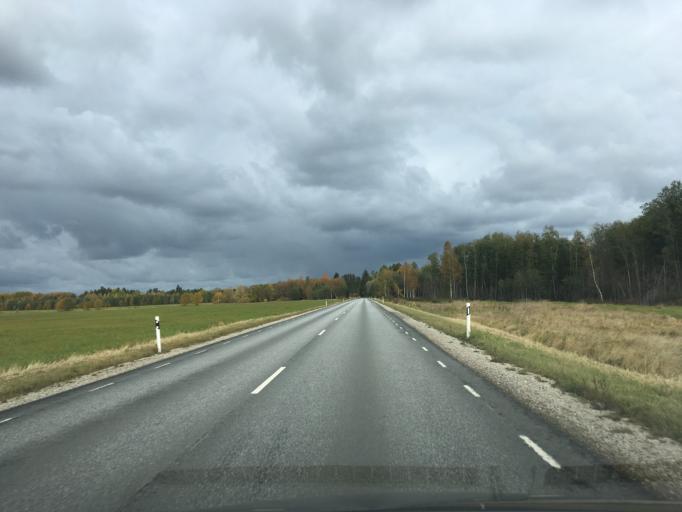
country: EE
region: Harju
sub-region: Anija vald
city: Kehra
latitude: 59.2868
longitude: 25.3749
